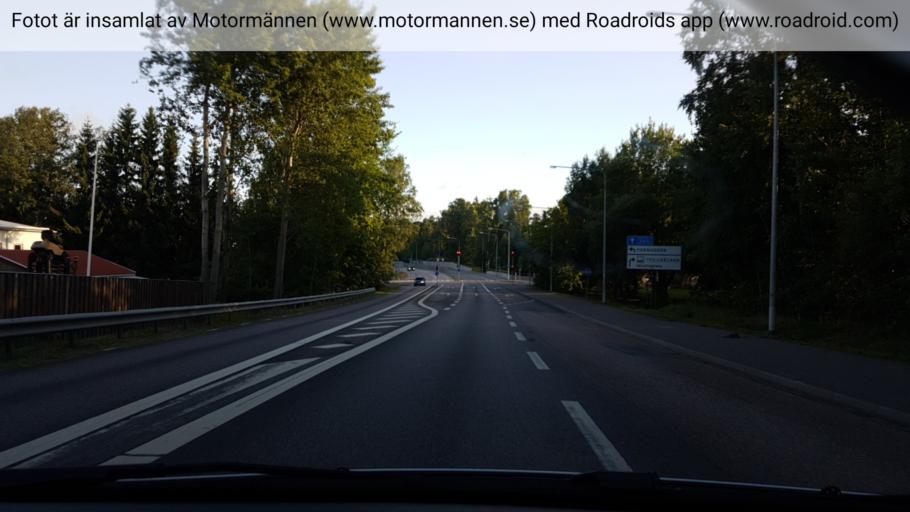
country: SE
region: Stockholm
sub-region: Tyreso Kommun
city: Bollmora
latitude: 59.2266
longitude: 18.2008
